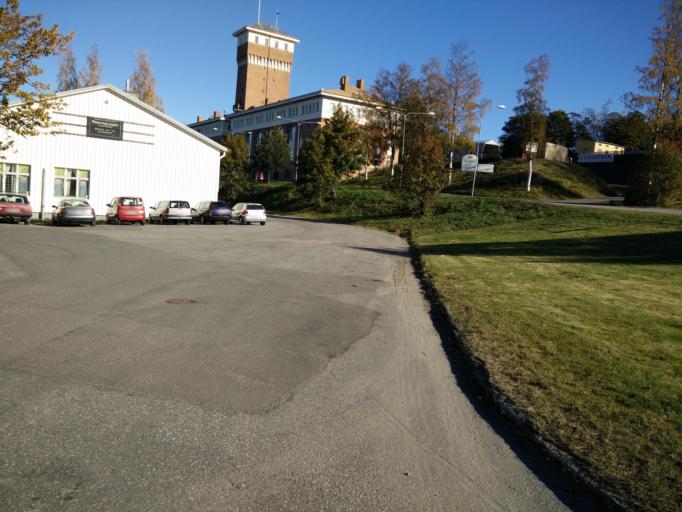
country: SE
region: Vaesternorrland
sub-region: Haernoesands Kommun
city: Haernoesand
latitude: 62.6392
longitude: 17.9497
